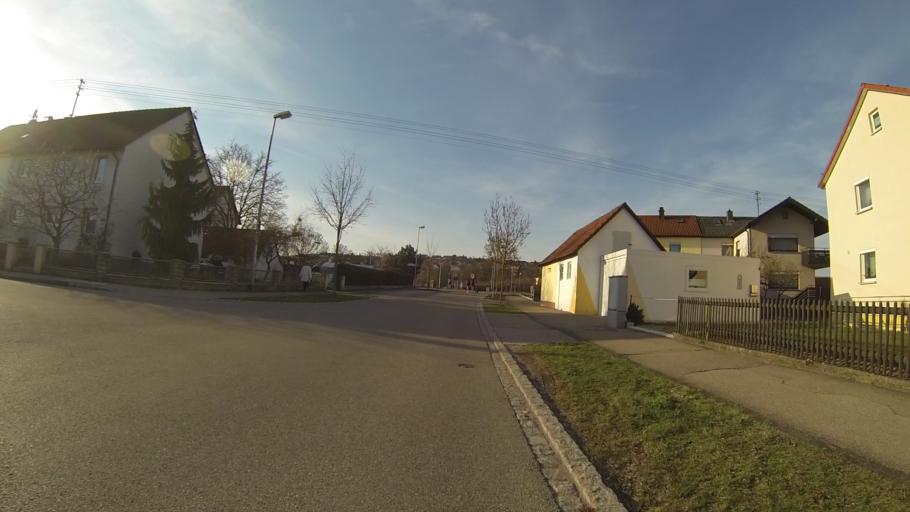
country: DE
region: Baden-Wuerttemberg
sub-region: Regierungsbezirk Stuttgart
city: Herbrechtingen
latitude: 48.6279
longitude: 10.1788
